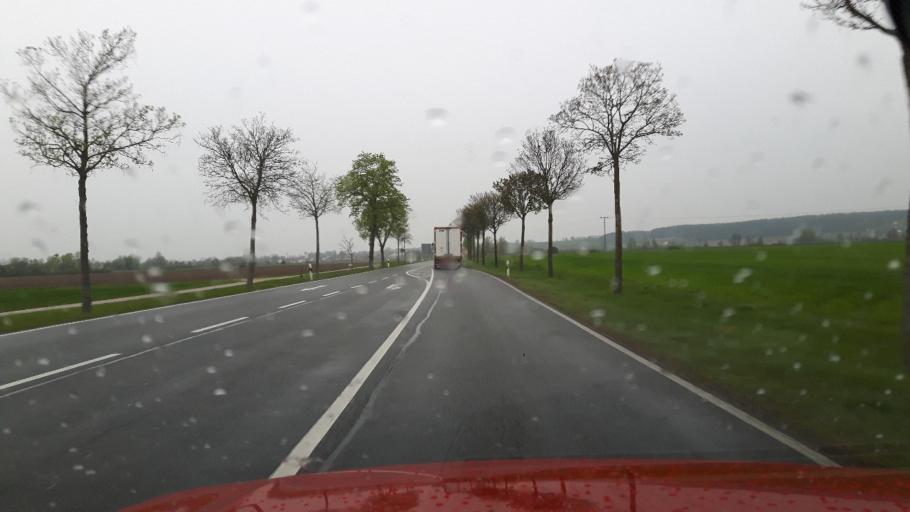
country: DE
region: Bavaria
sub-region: Regierungsbezirk Mittelfranken
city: Muhr am See
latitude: 49.1371
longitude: 10.7399
